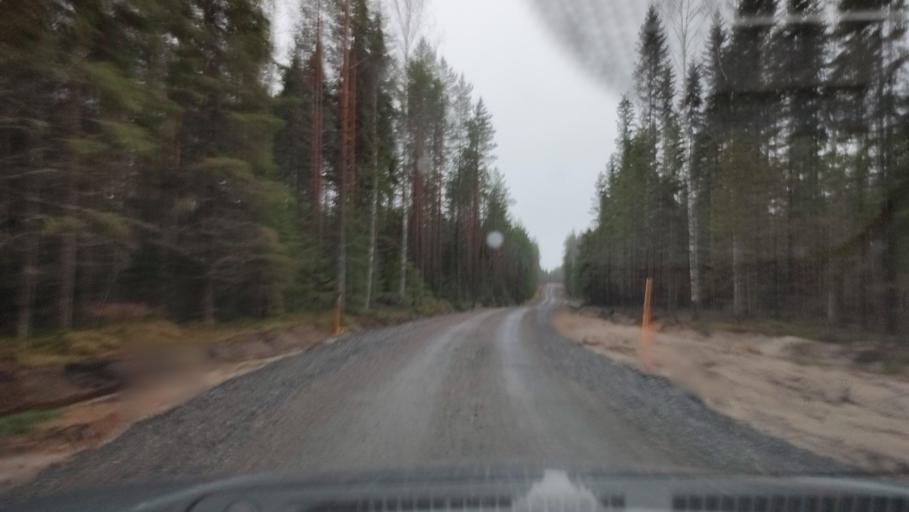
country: FI
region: Southern Ostrobothnia
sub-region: Suupohja
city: Karijoki
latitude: 62.1489
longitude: 21.6324
